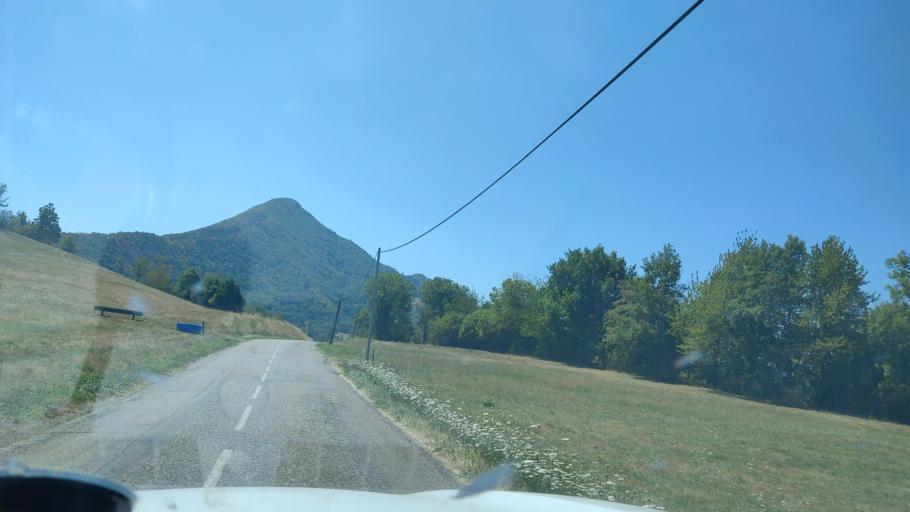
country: FR
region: Rhone-Alpes
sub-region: Departement de la Savoie
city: Barby
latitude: 45.5653
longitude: 6.0240
